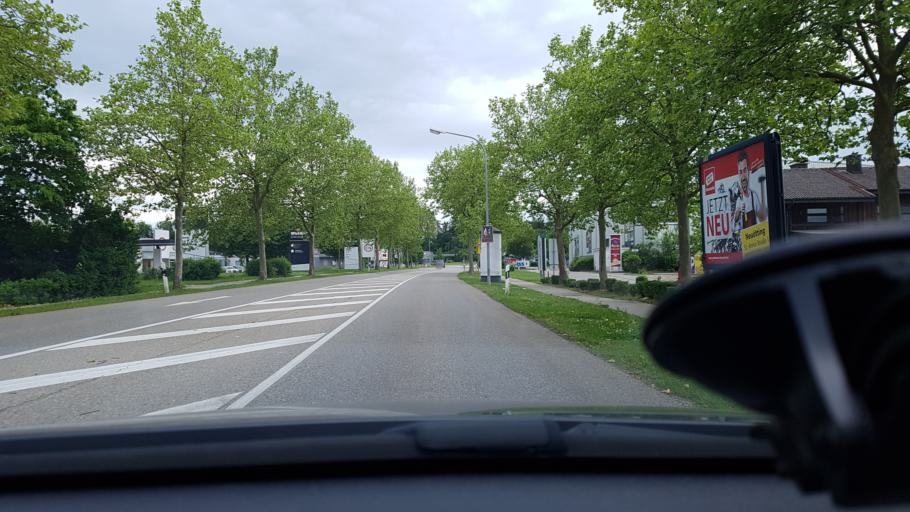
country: DE
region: Bavaria
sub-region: Upper Bavaria
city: Neuotting
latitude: 48.2425
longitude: 12.7088
